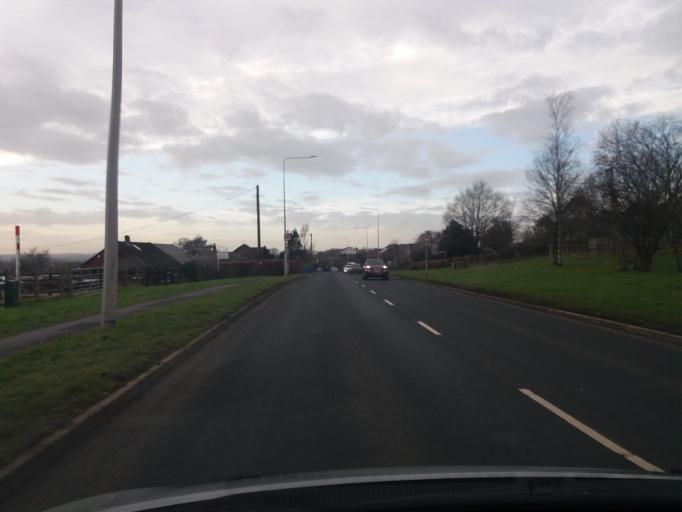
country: GB
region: England
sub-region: Borough of Wigan
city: Haigh
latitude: 53.6126
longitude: -2.5842
